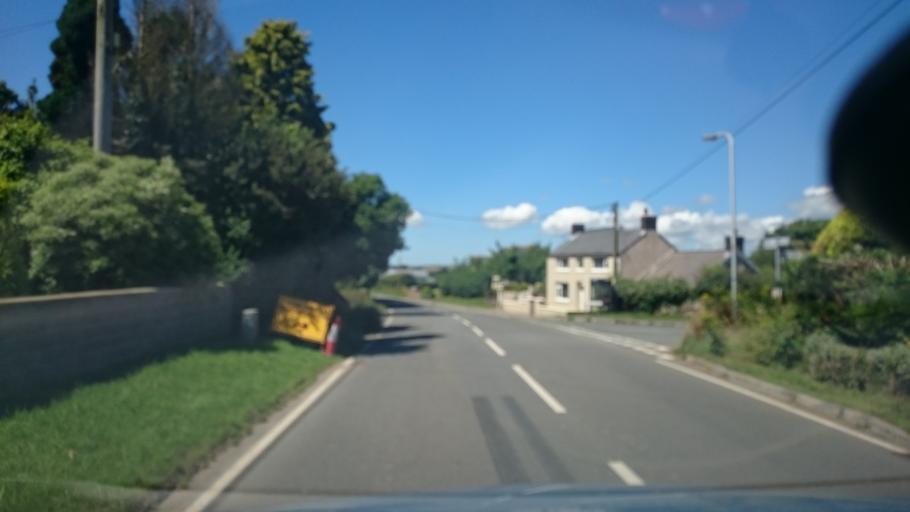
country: GB
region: Wales
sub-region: Pembrokeshire
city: Llangwm
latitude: 51.7367
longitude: -4.9296
